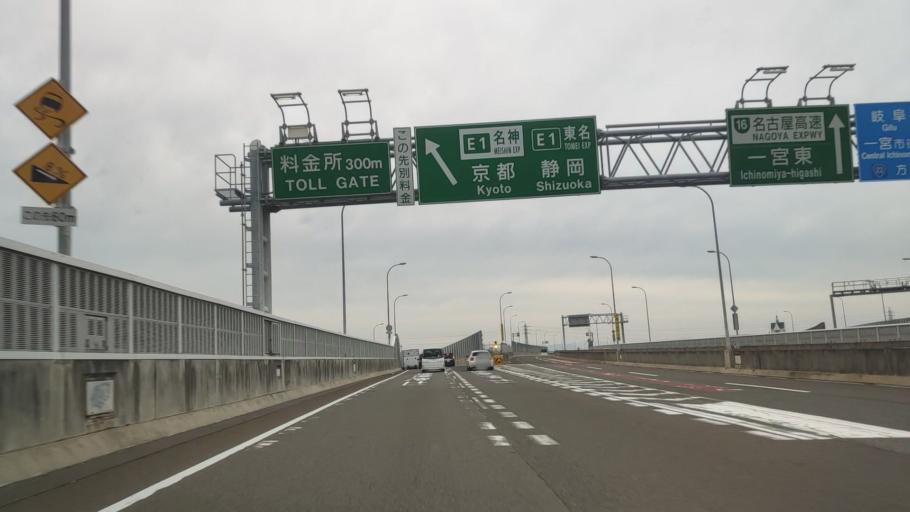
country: JP
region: Aichi
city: Iwakura
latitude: 35.2694
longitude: 136.8328
